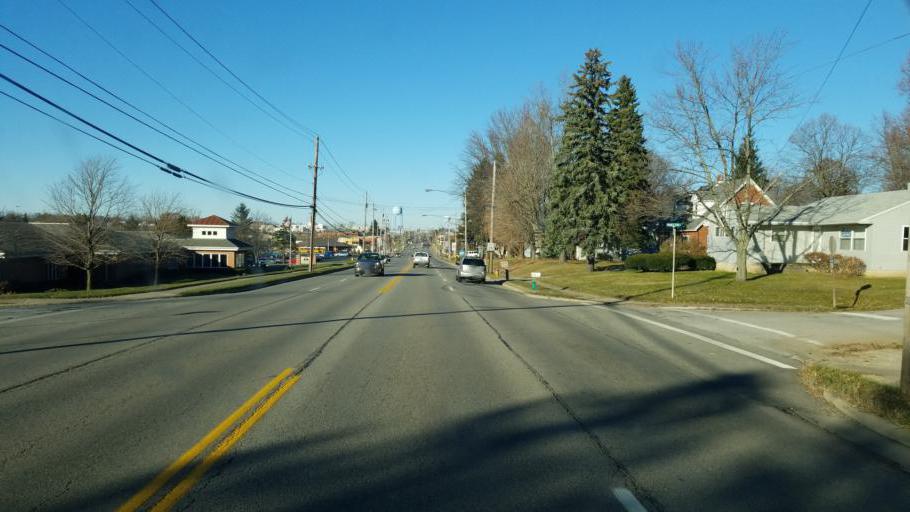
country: US
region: Ohio
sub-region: Richland County
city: Ontario
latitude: 40.7566
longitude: -82.5903
